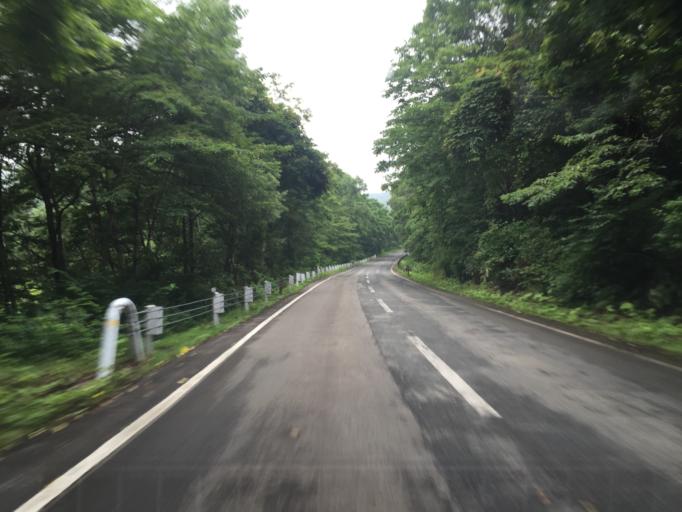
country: JP
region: Fukushima
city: Inawashiro
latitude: 37.6651
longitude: 140.0919
